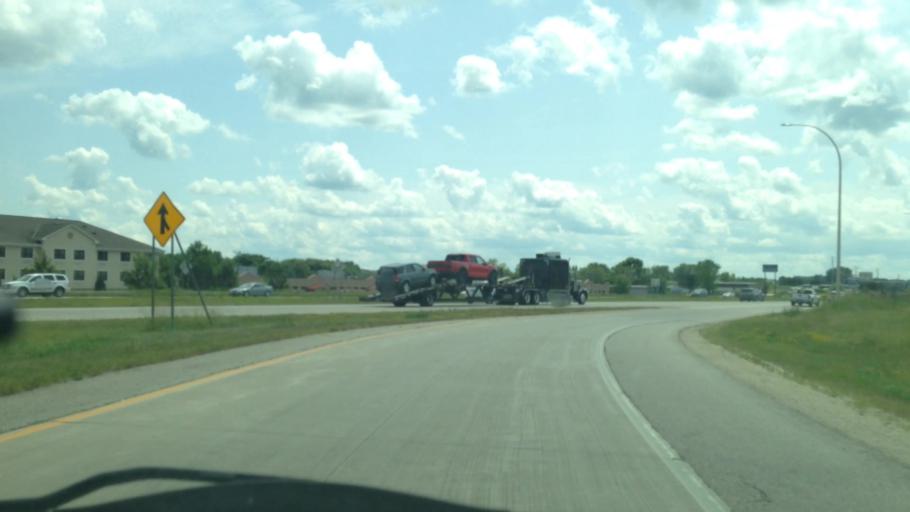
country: US
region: Minnesota
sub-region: Olmsted County
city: Rochester
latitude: 43.9749
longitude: -92.4635
